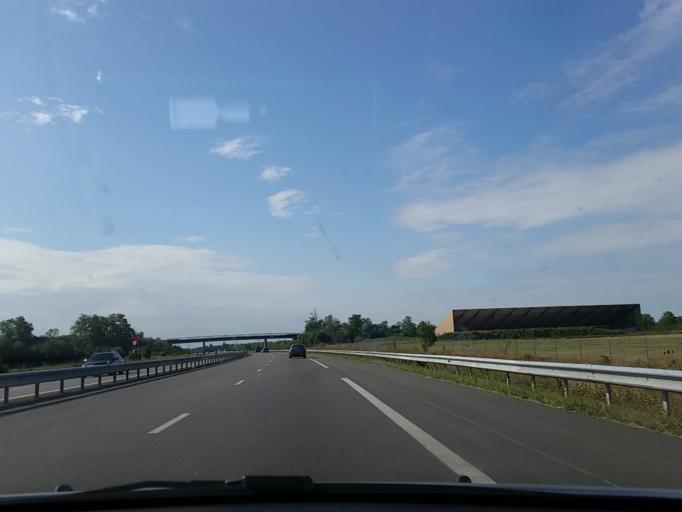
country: FR
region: Centre
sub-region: Departement du Cher
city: Levet
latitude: 46.9080
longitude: 2.4175
